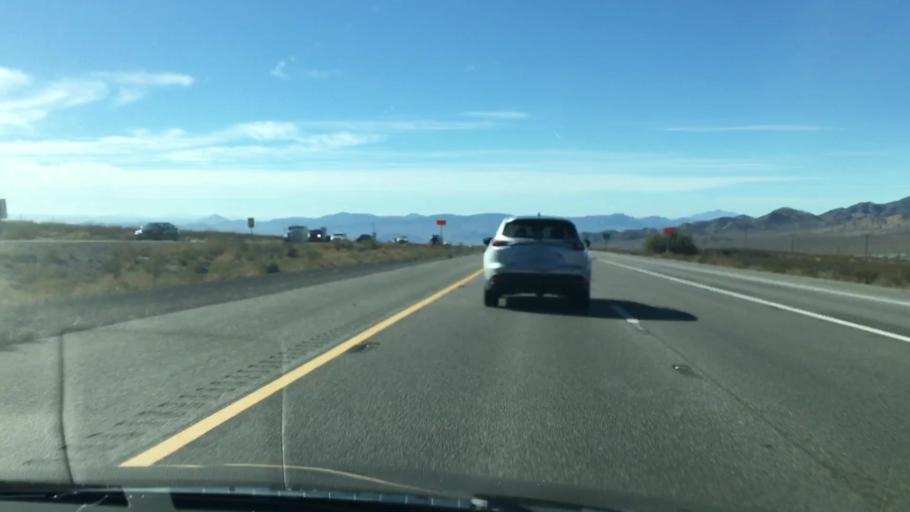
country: US
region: Nevada
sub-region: Clark County
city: Sandy Valley
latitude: 35.3774
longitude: -115.8825
